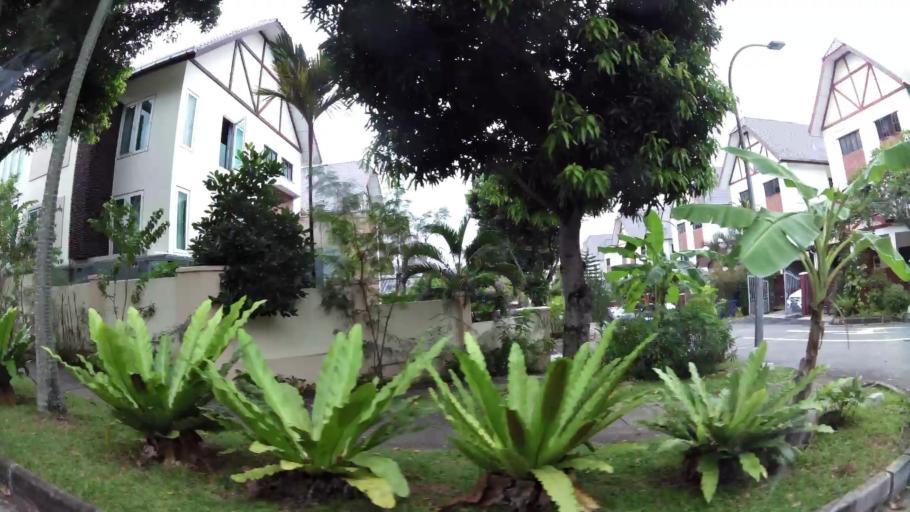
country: SG
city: Singapore
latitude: 1.3589
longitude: 103.8799
